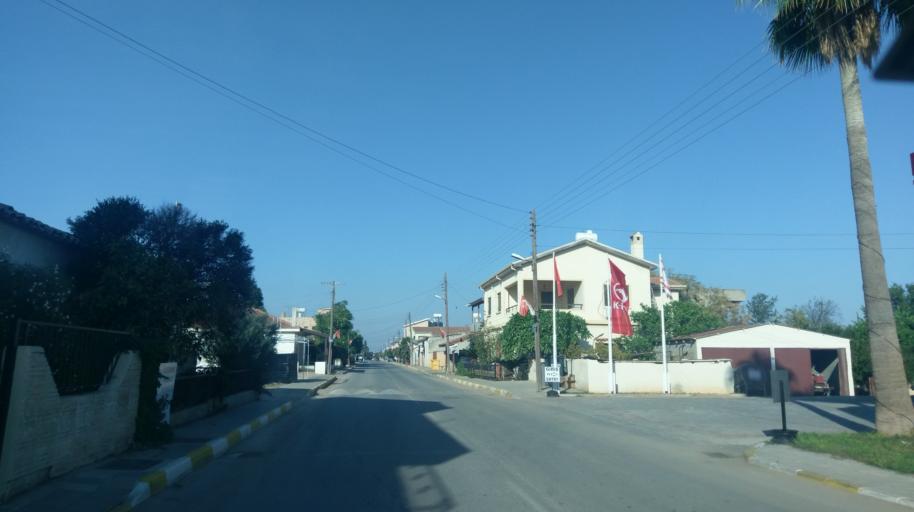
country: CY
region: Larnaka
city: Pergamos
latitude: 35.0420
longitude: 33.7079
